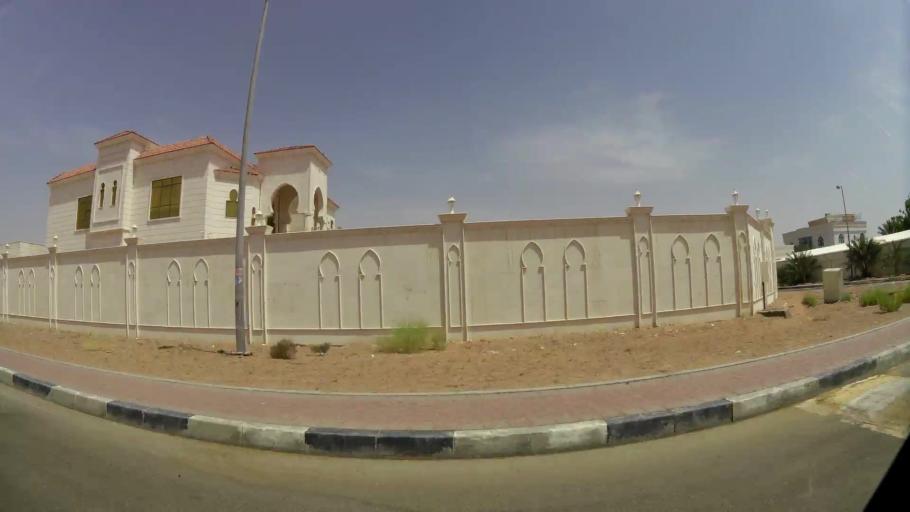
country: AE
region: Abu Dhabi
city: Al Ain
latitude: 24.1786
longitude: 55.7113
